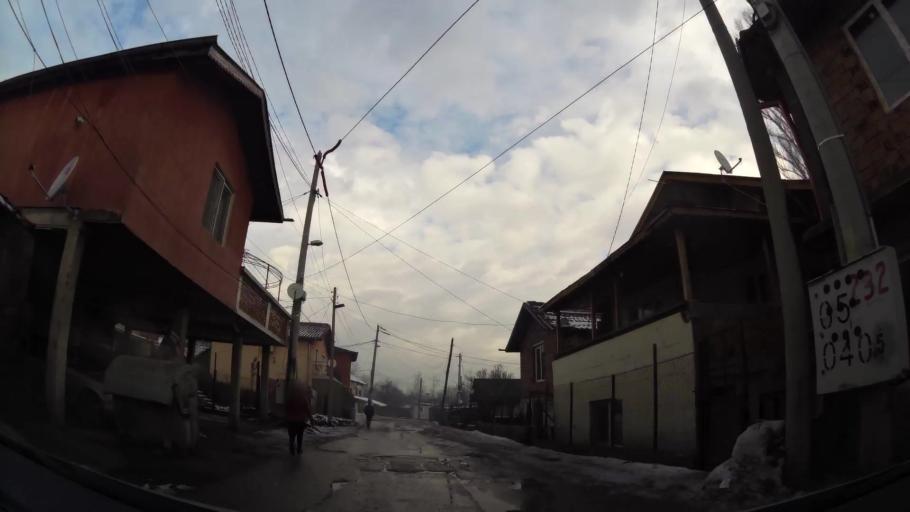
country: BG
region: Sofia-Capital
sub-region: Stolichna Obshtina
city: Sofia
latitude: 42.6965
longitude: 23.2665
